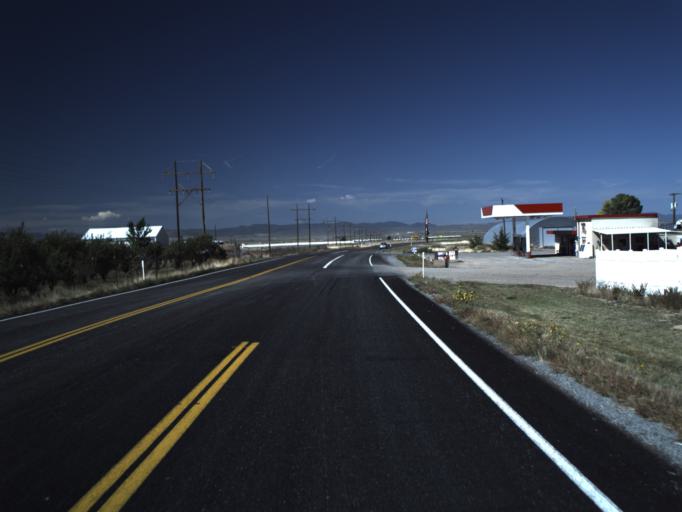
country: US
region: Utah
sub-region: Washington County
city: Enterprise
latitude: 37.6722
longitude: -113.5477
